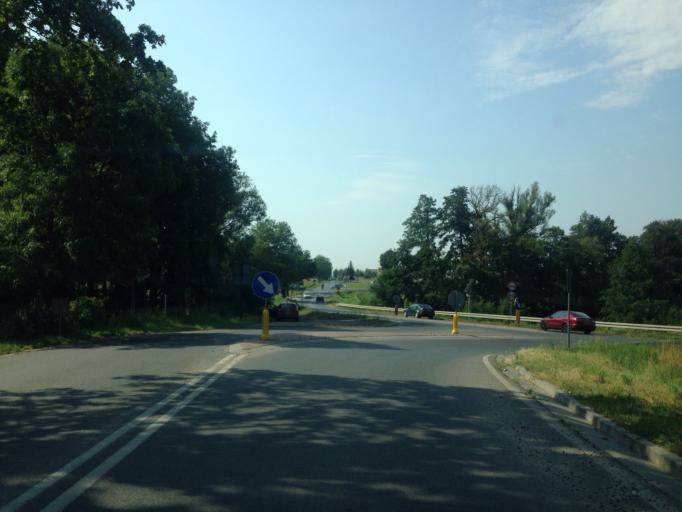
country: PL
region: Kujawsko-Pomorskie
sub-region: Powiat rypinski
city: Rypin
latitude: 53.0860
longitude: 19.4158
